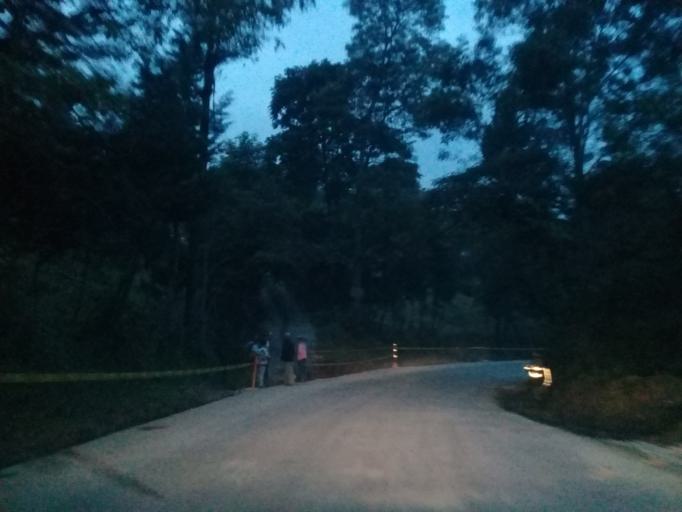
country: CO
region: Cundinamarca
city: Pacho
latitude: 5.1331
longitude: -74.1423
